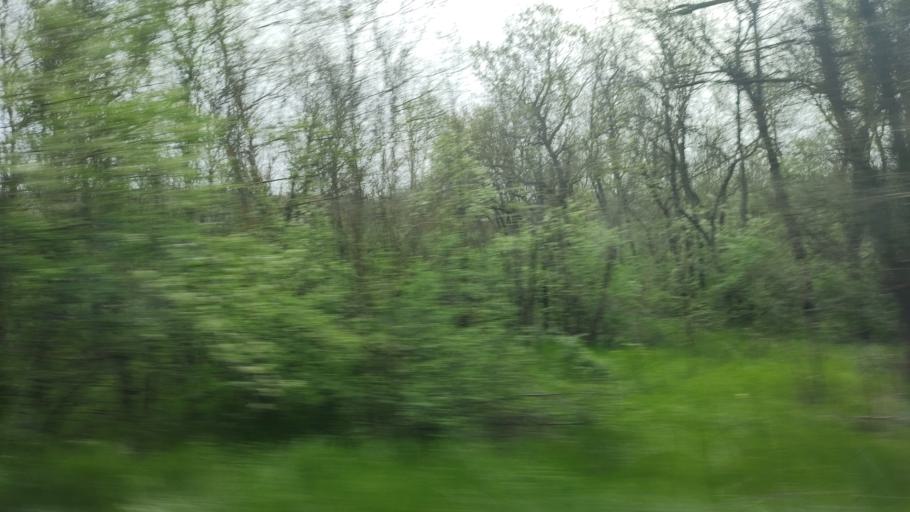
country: RO
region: Constanta
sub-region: Oras Murfatlar
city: Siminoc
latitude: 44.1526
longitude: 28.3750
